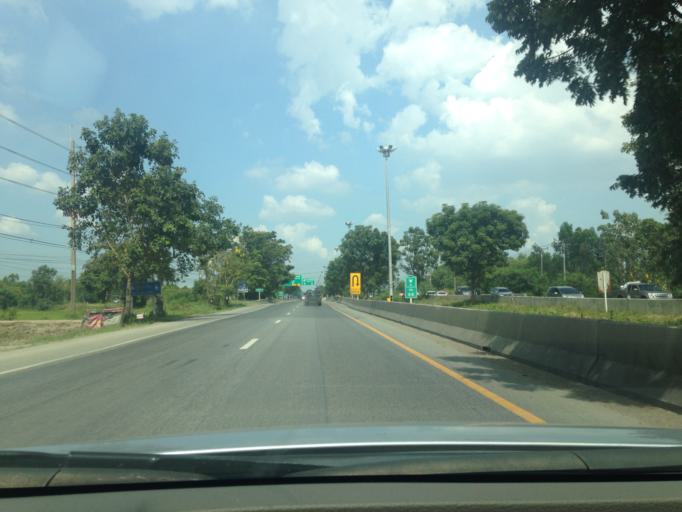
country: TH
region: Pathum Thani
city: Sam Khok
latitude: 14.0870
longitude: 100.5108
